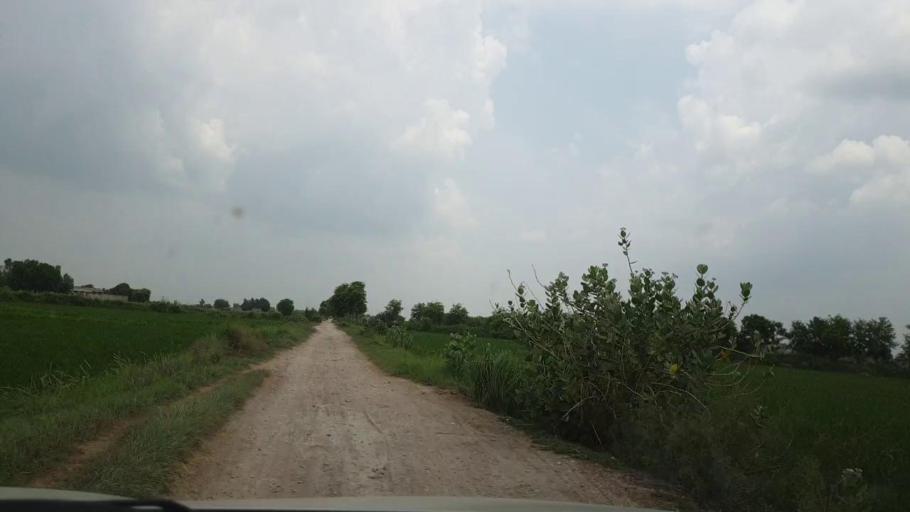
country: PK
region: Sindh
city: Goth Garelo
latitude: 27.4292
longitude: 68.0845
